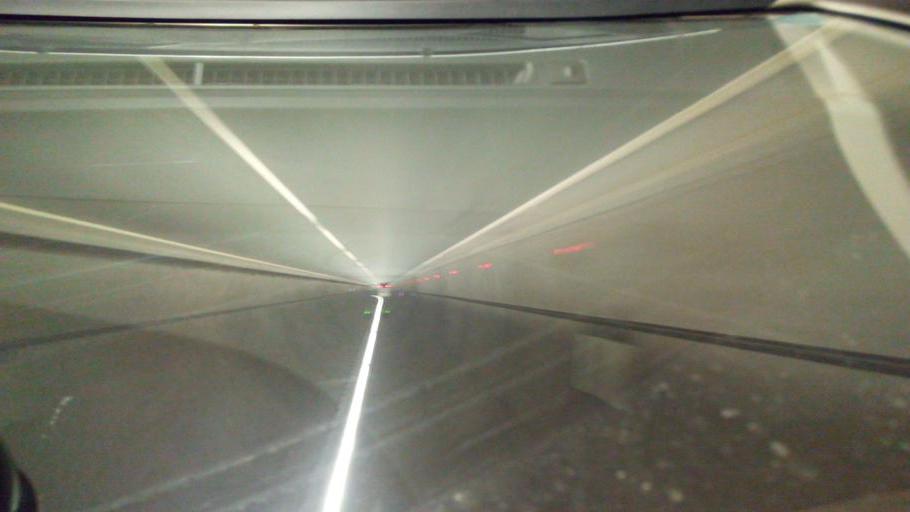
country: CY
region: Limassol
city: Sotira
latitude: 34.6990
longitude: 32.8402
